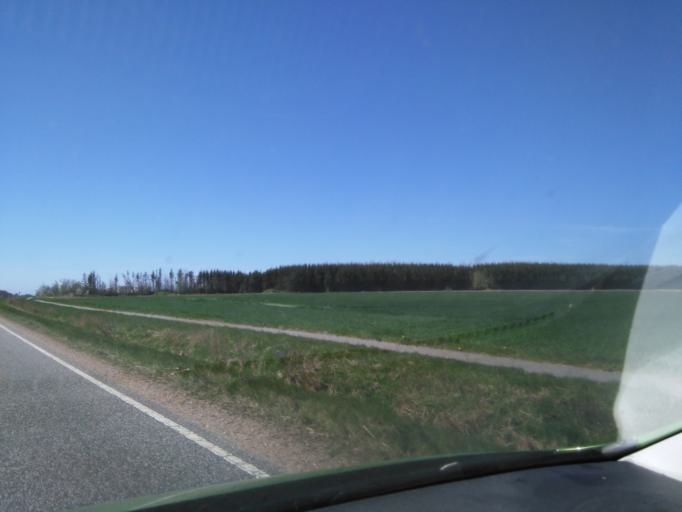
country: DK
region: South Denmark
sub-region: Varde Kommune
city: Oksbol
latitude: 55.6210
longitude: 8.3584
